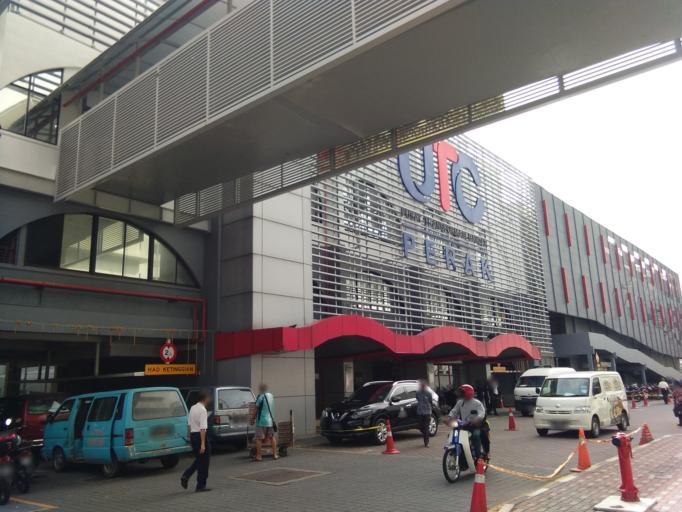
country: MY
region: Perak
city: Ipoh
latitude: 4.5956
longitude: 101.0820
